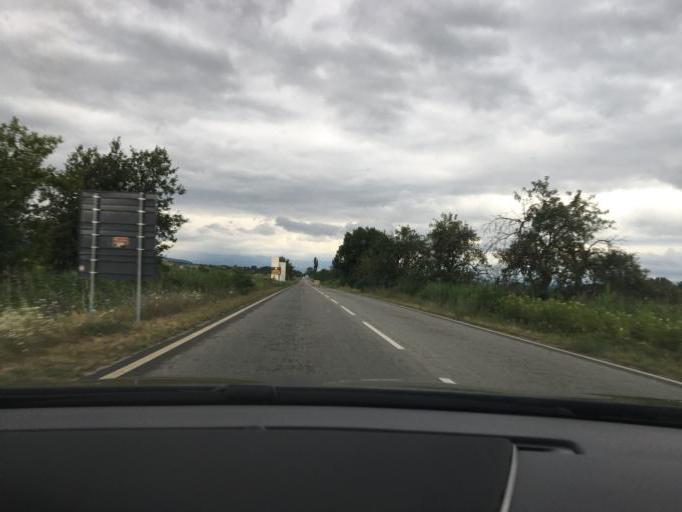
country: BG
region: Kyustendil
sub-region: Obshtina Kyustendil
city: Kyustendil
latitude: 42.2628
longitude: 22.8232
